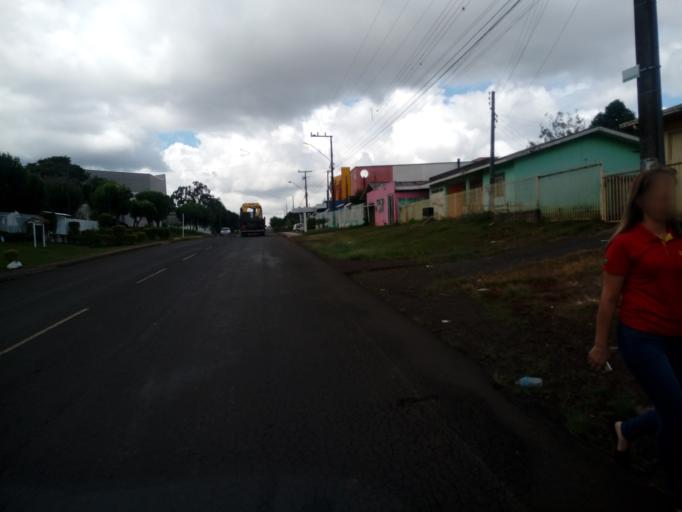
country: BR
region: Santa Catarina
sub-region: Chapeco
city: Chapeco
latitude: -27.0828
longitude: -52.6080
